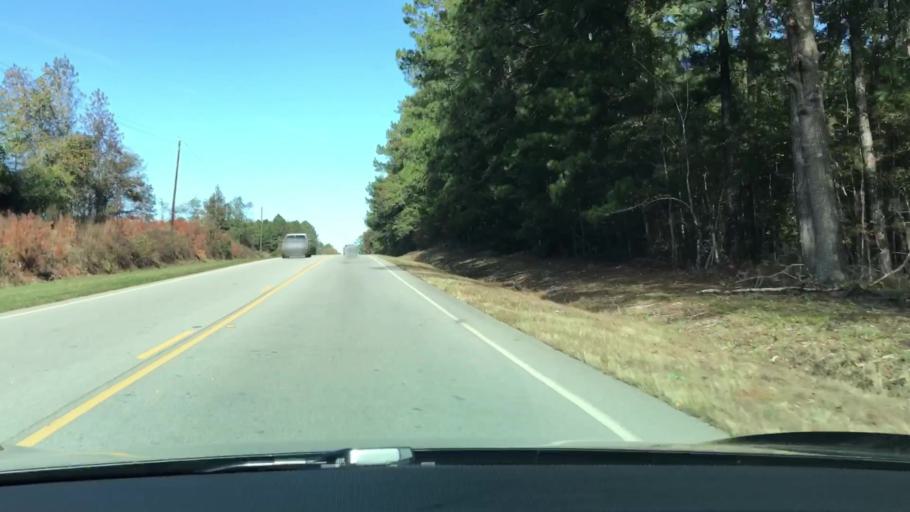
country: US
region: Georgia
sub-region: Warren County
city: Firing Range
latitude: 33.4330
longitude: -82.6872
